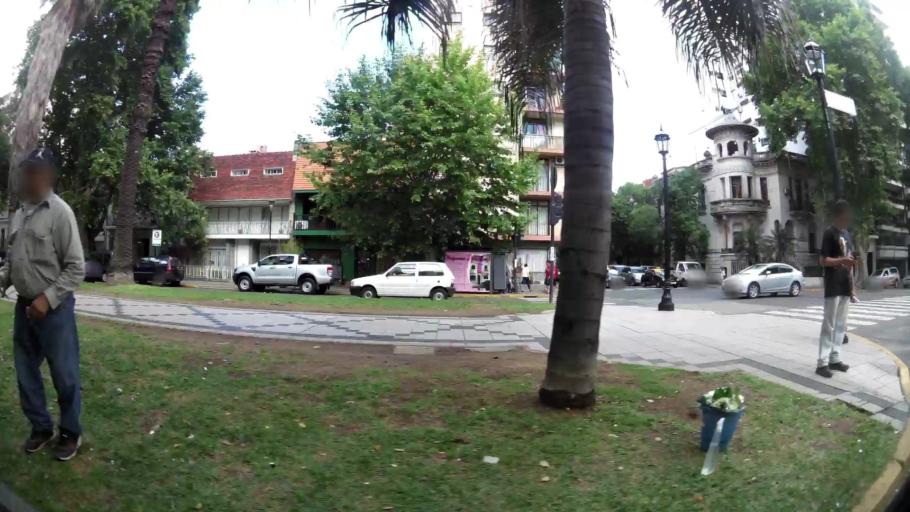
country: AR
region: Santa Fe
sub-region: Departamento de Rosario
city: Rosario
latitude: -32.9490
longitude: -60.6546
